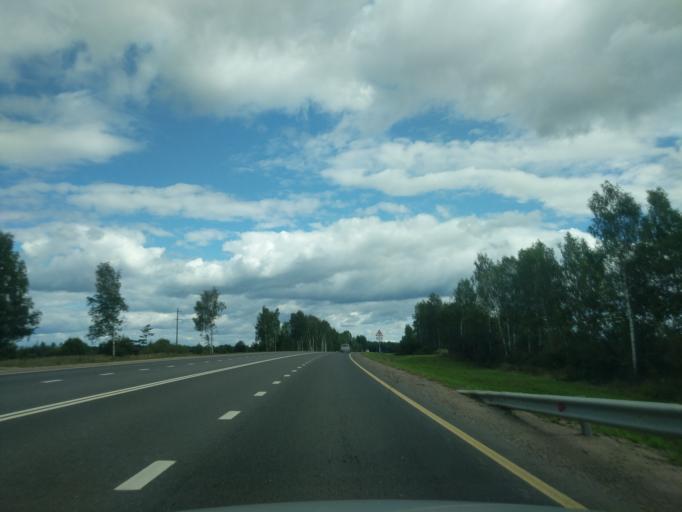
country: RU
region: Kostroma
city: Oktyabr'skiy
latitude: 57.7858
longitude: 41.1002
